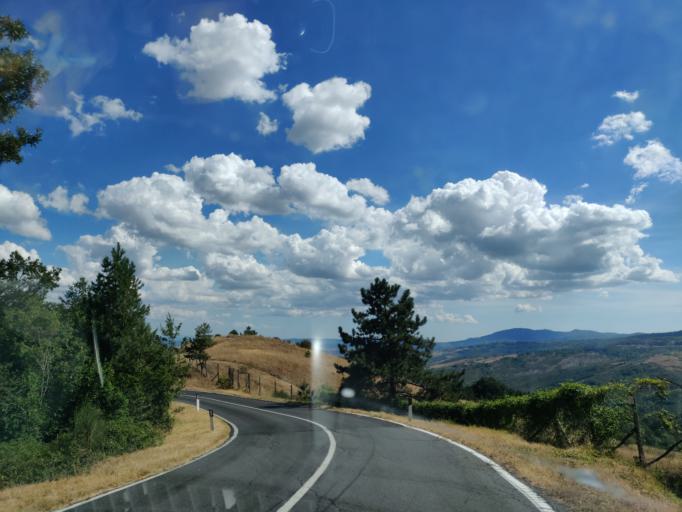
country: IT
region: Tuscany
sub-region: Provincia di Siena
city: Abbadia San Salvatore
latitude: 42.9086
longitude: 11.6933
